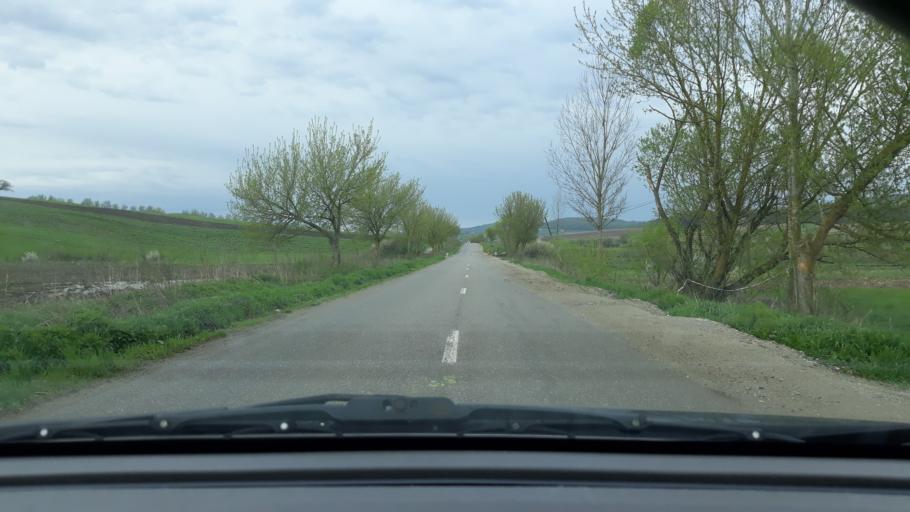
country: RO
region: Salaj
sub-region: Comuna Salatig
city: Salatig
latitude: 47.3818
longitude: 23.1465
